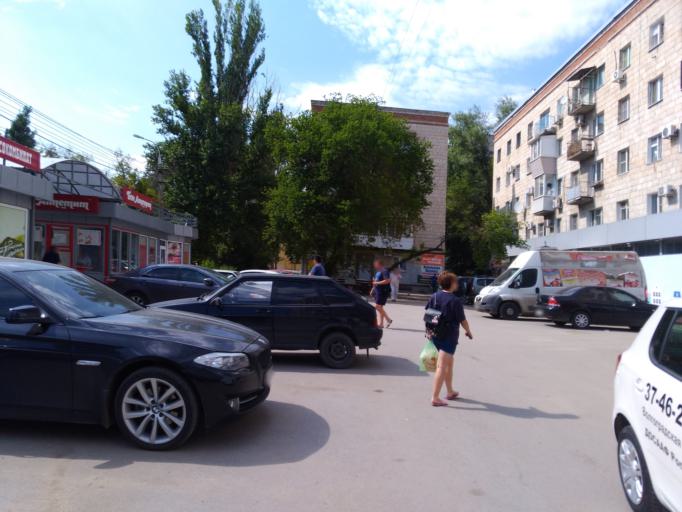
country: RU
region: Volgograd
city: Volgograd
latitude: 48.7131
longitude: 44.5001
